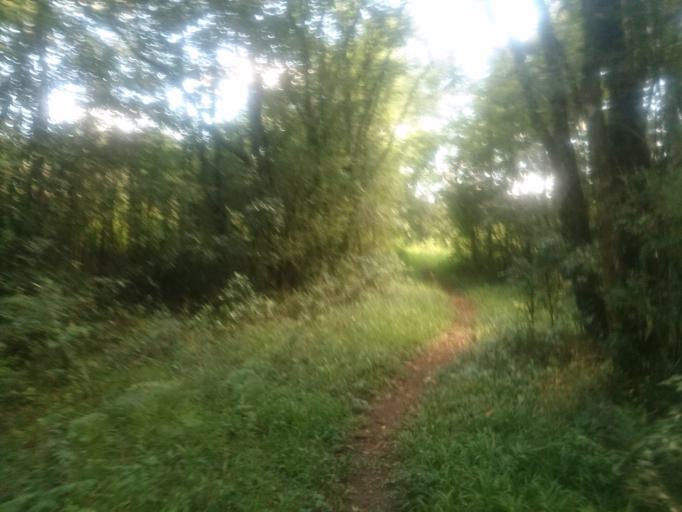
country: AR
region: Misiones
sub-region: Departamento de Obera
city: Obera
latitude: -27.4455
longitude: -55.1108
